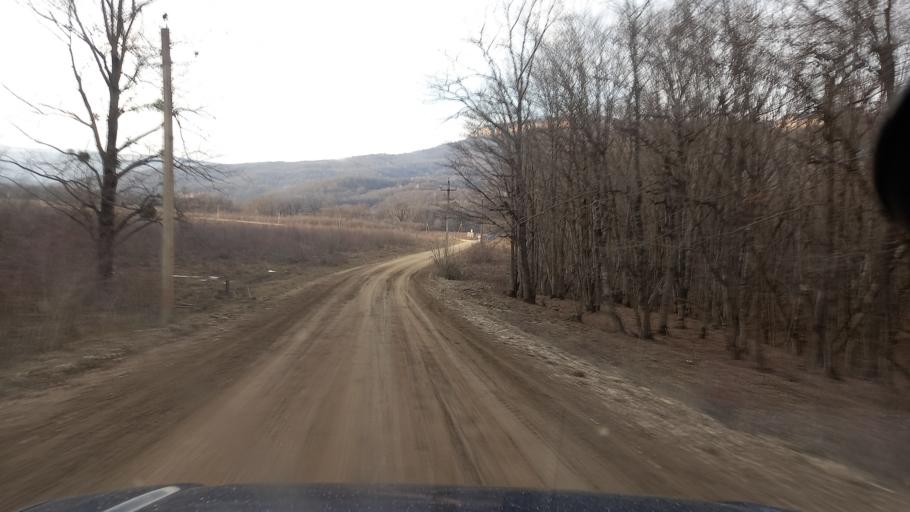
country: RU
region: Adygeya
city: Kamennomostskiy
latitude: 44.2099
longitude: 40.2543
